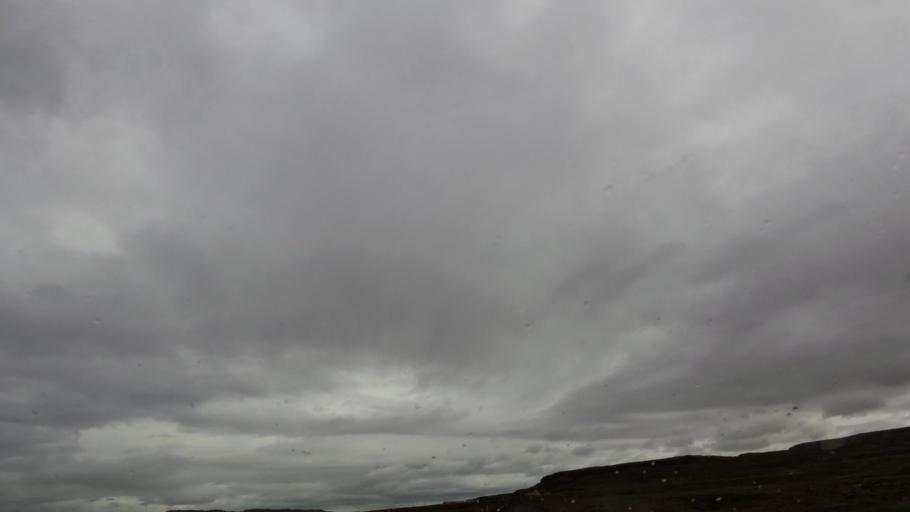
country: IS
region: West
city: Borgarnes
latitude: 65.0250
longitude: -22.1099
